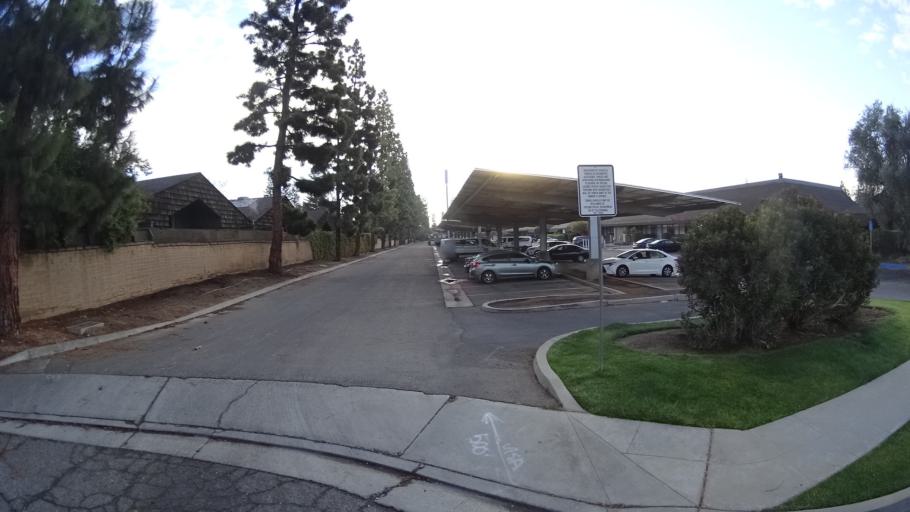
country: US
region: California
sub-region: Fresno County
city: Fresno
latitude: 36.8091
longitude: -119.8354
